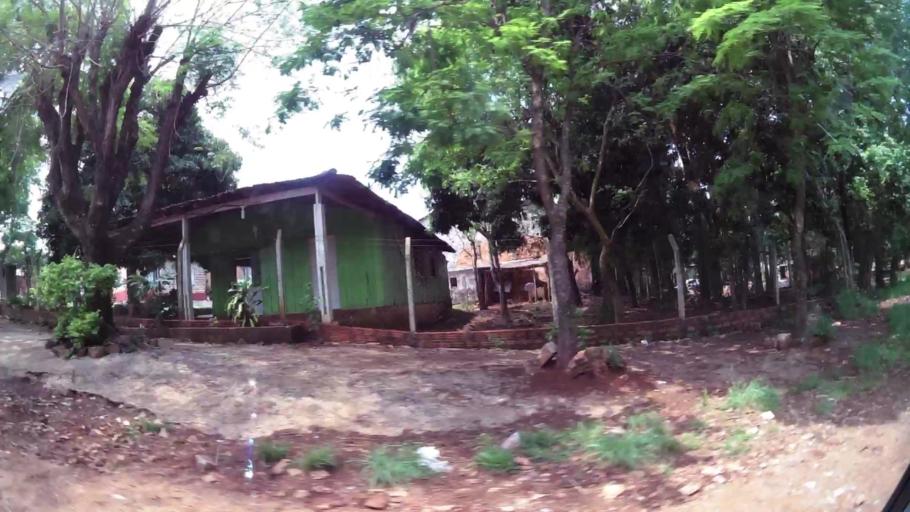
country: PY
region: Alto Parana
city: Ciudad del Este
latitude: -25.4985
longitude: -54.6286
